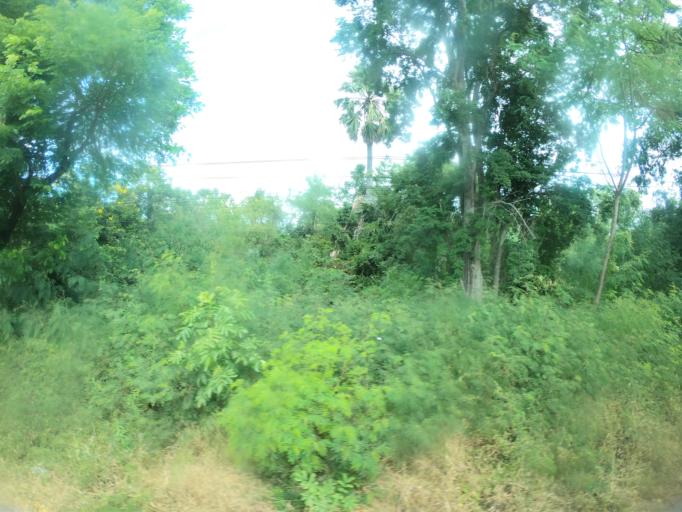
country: TH
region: Maha Sarakham
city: Chiang Yuen
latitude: 16.3441
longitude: 103.1296
